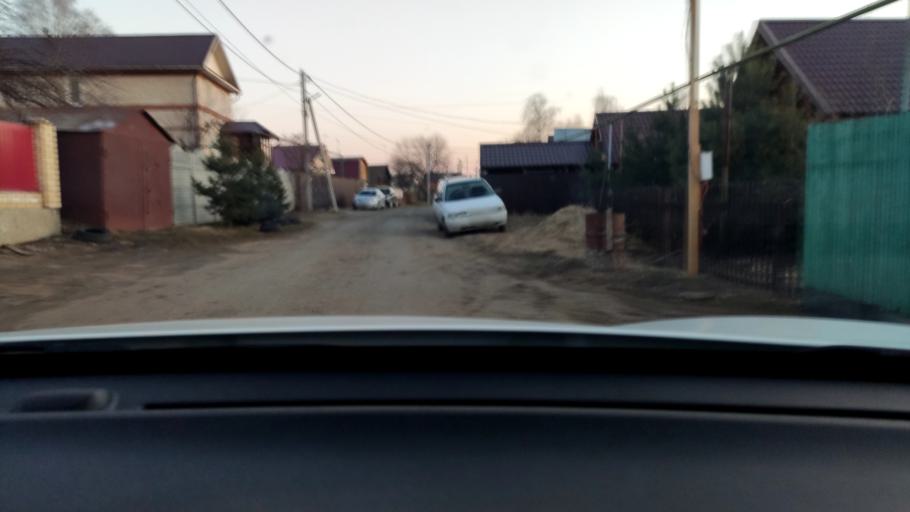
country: RU
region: Tatarstan
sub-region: Gorod Kazan'
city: Kazan
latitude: 55.7318
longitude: 49.1541
